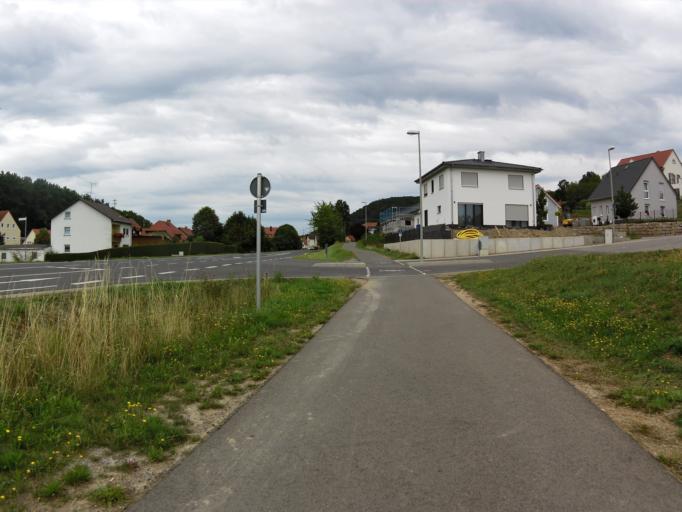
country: DE
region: Bavaria
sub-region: Regierungsbezirk Unterfranken
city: Sand
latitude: 49.9850
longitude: 10.6229
